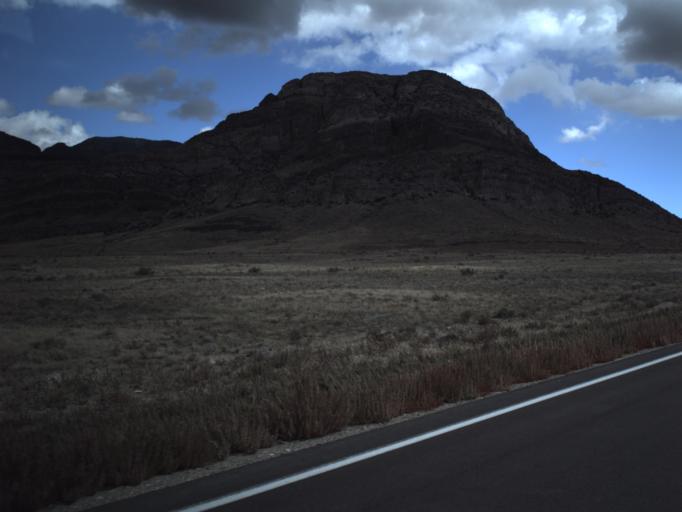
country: US
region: Utah
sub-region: Beaver County
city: Milford
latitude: 38.5060
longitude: -113.6088
